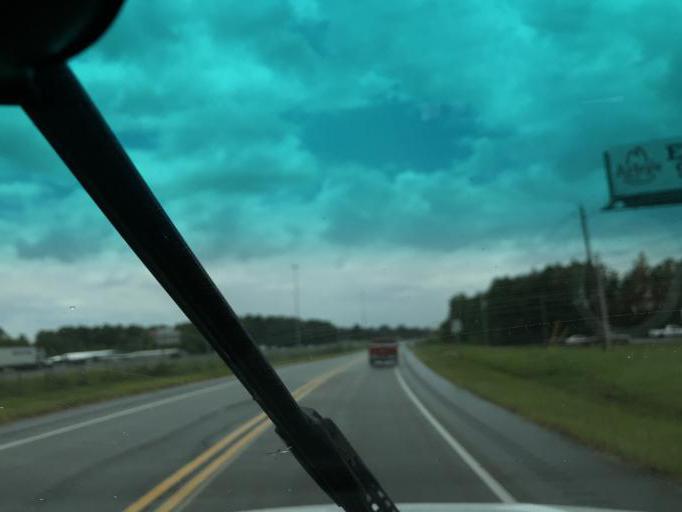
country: US
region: Alabama
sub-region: Montgomery County
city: Pike Road
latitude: 32.3676
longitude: -86.0883
